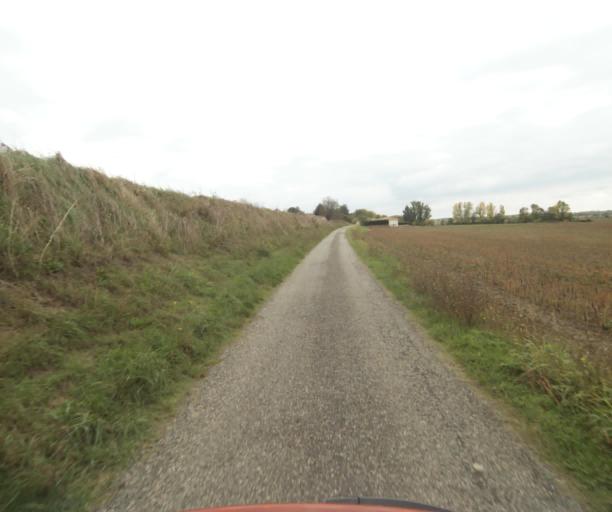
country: FR
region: Midi-Pyrenees
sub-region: Departement du Tarn-et-Garonne
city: Finhan
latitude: 43.8970
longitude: 1.2310
